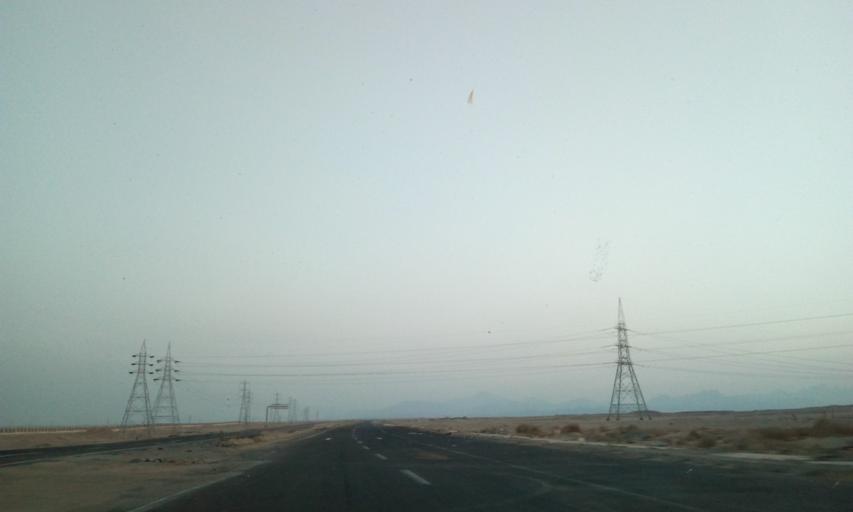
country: EG
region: Red Sea
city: El Gouna
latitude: 27.3270
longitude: 33.6659
